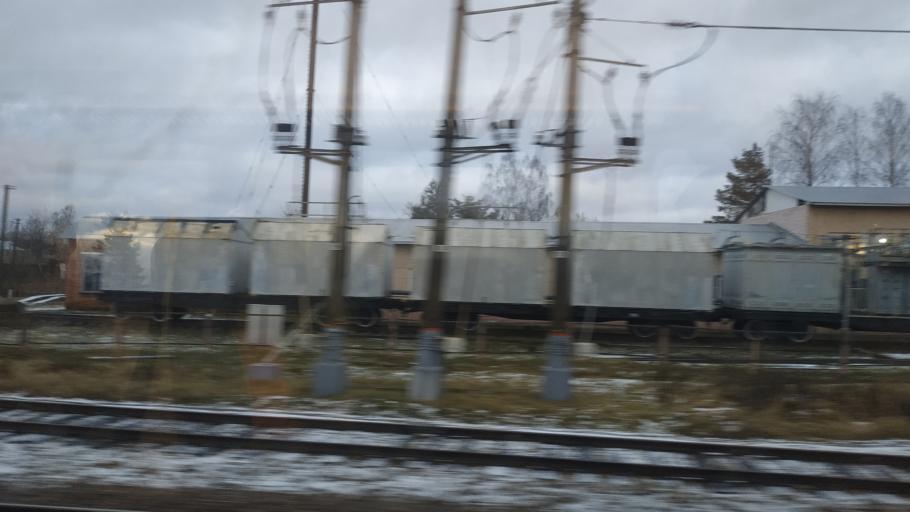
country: RU
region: Moskovskaya
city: Taldom
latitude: 56.7202
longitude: 37.5304
